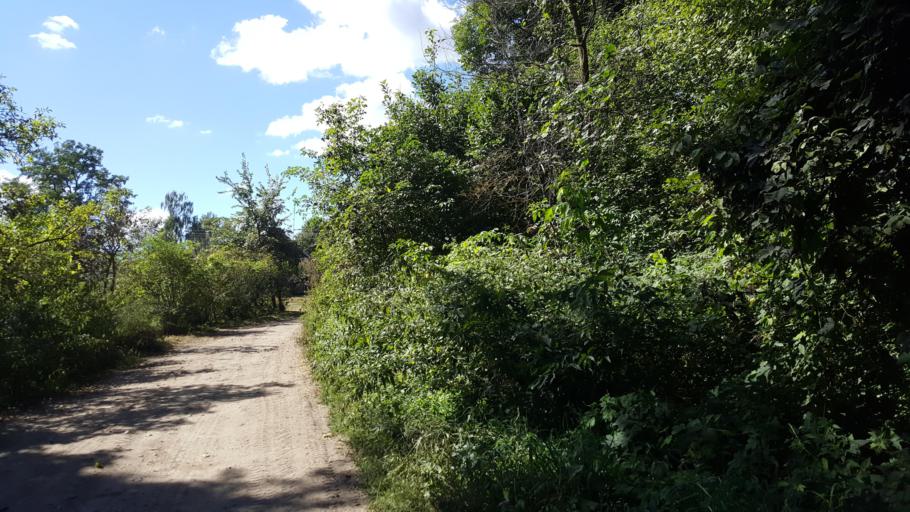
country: BY
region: Brest
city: Vysokaye
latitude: 52.3317
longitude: 23.3482
